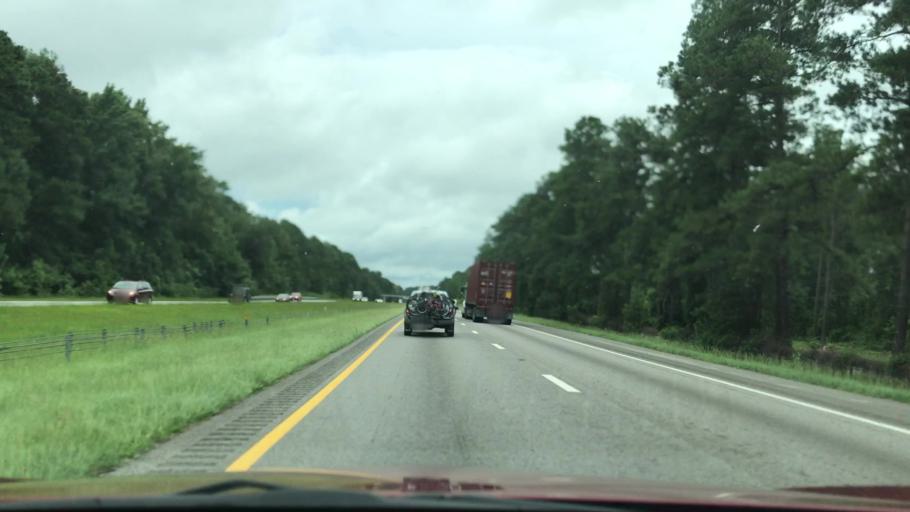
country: US
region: South Carolina
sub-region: Orangeburg County
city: Brookdale
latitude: 33.5385
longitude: -80.8074
